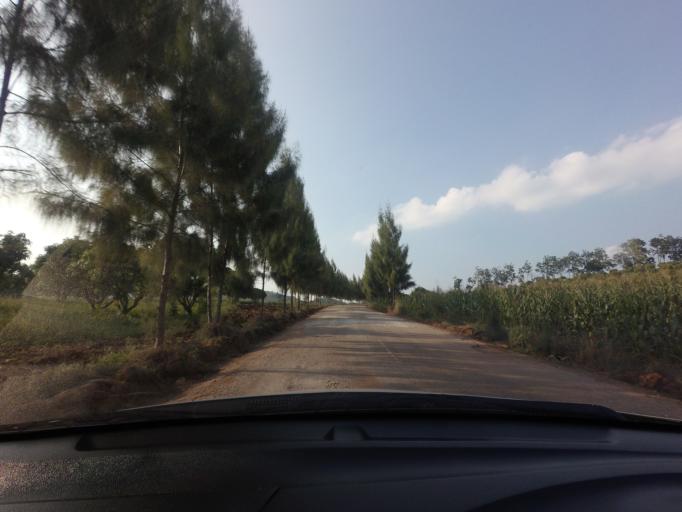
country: TH
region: Nakhon Ratchasima
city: Pak Chong
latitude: 14.5480
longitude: 101.5755
